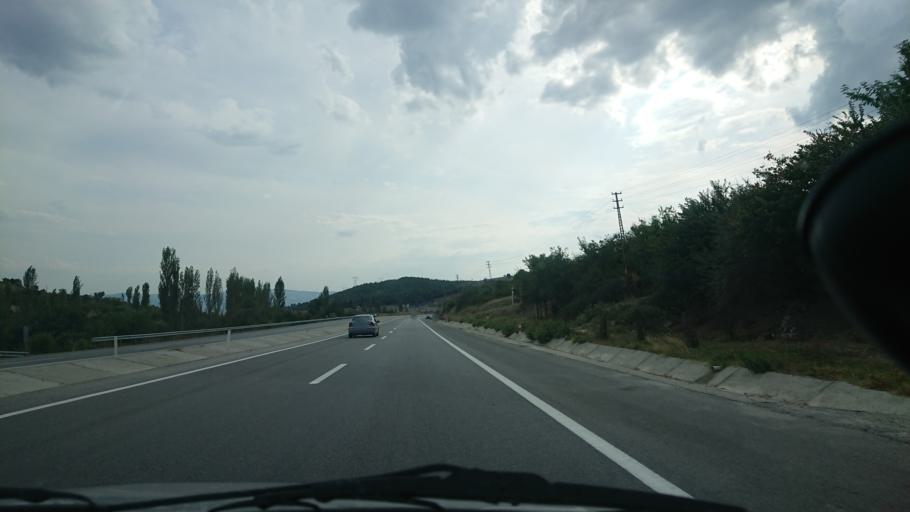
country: TR
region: Kuetahya
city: Gediz
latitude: 39.0377
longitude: 29.4214
